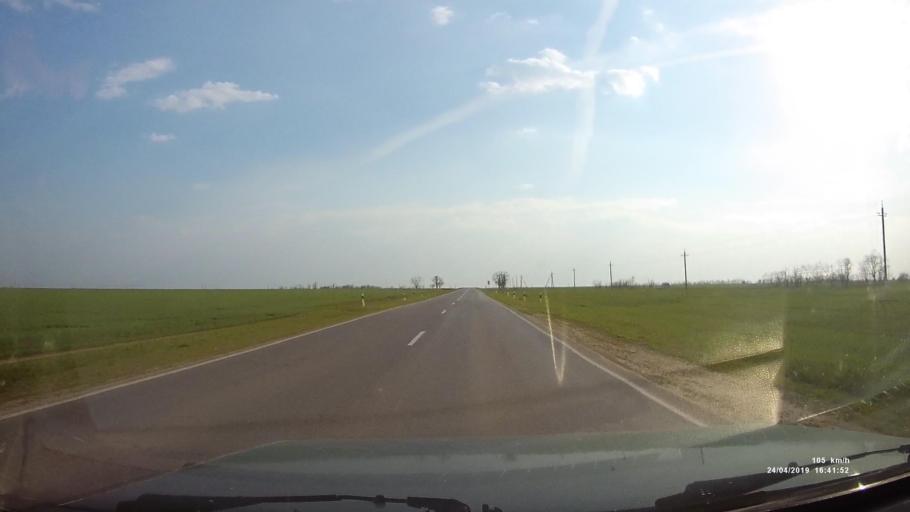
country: RU
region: Rostov
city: Gundorovskiy
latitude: 46.8146
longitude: 41.8617
